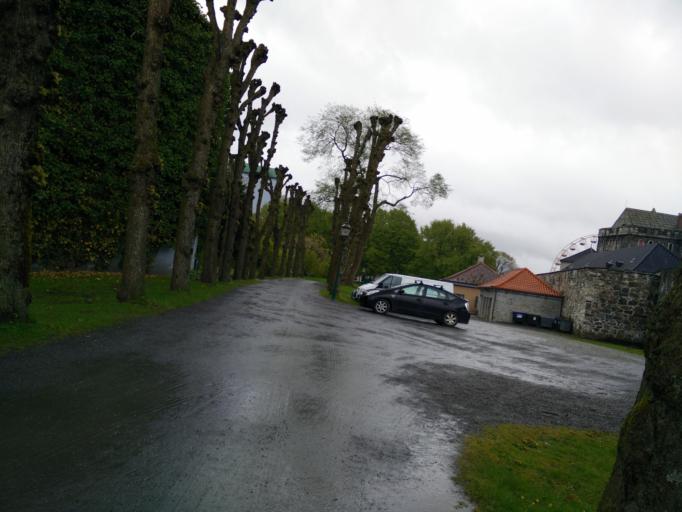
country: NO
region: Hordaland
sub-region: Bergen
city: Bergen
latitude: 60.4001
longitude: 5.3175
